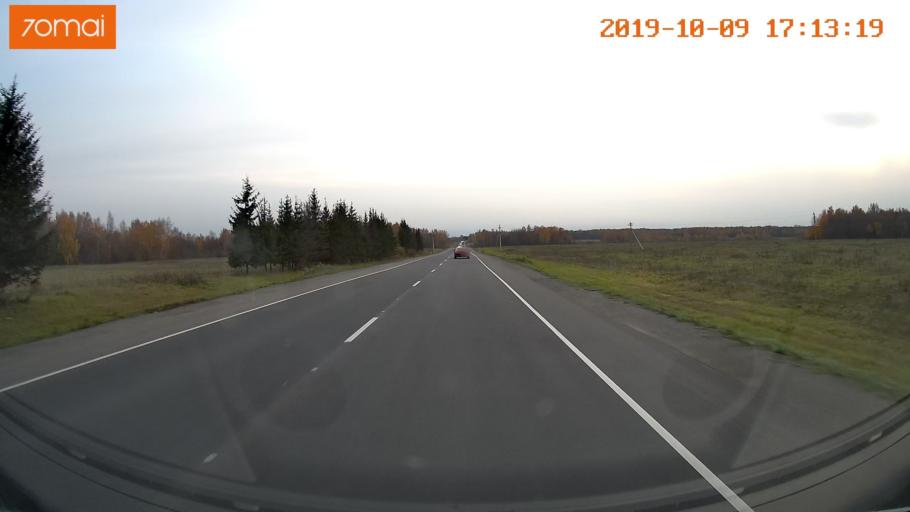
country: RU
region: Ivanovo
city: Privolzhsk
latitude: 57.3168
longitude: 41.2263
